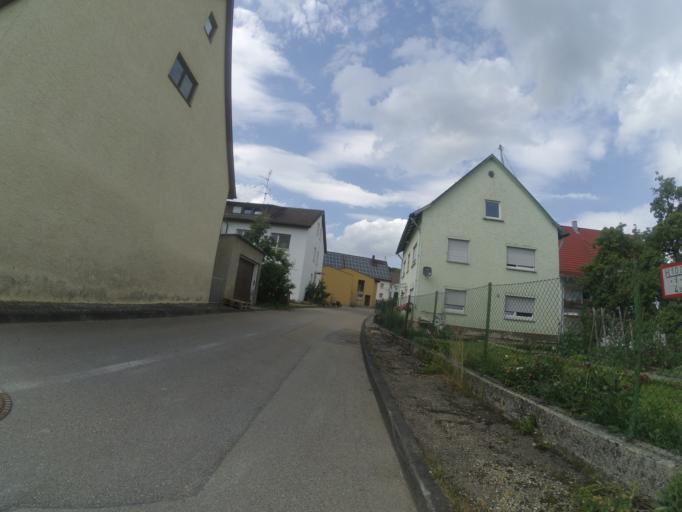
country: DE
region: Baden-Wuerttemberg
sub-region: Tuebingen Region
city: Griesingen
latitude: 48.2781
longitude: 9.7612
